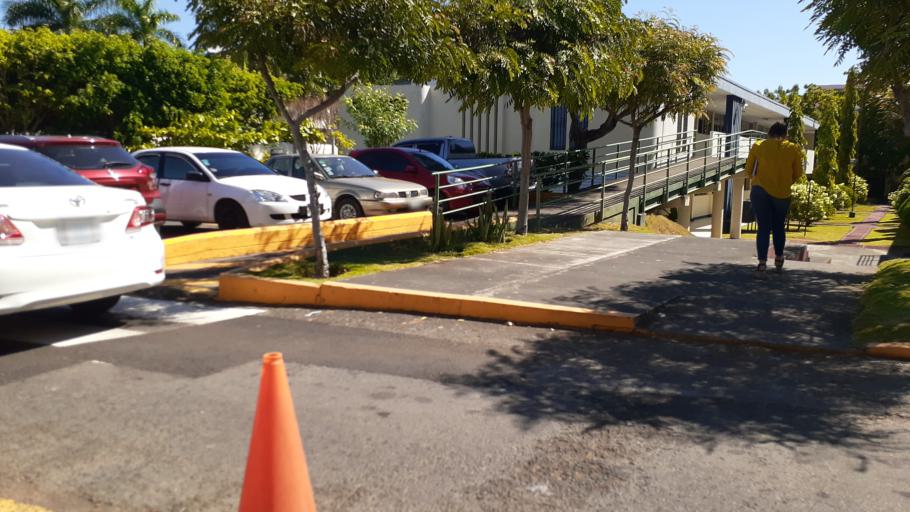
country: NI
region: Managua
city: Managua
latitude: 12.1250
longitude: -86.2720
